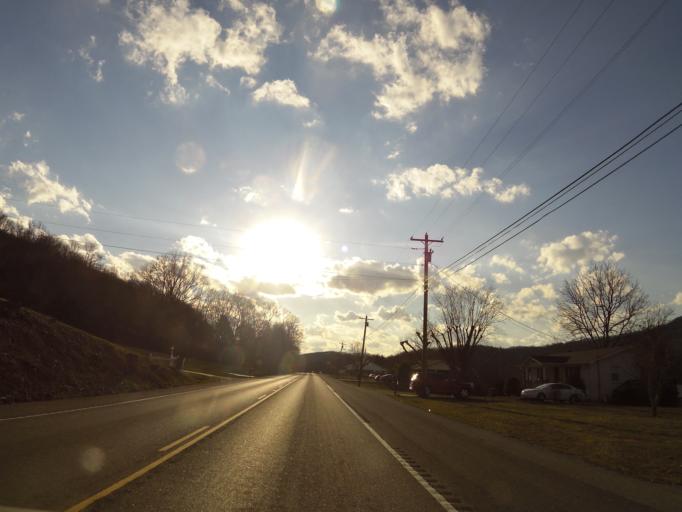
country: US
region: Tennessee
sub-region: Smith County
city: Carthage
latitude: 36.2541
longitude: -86.0049
